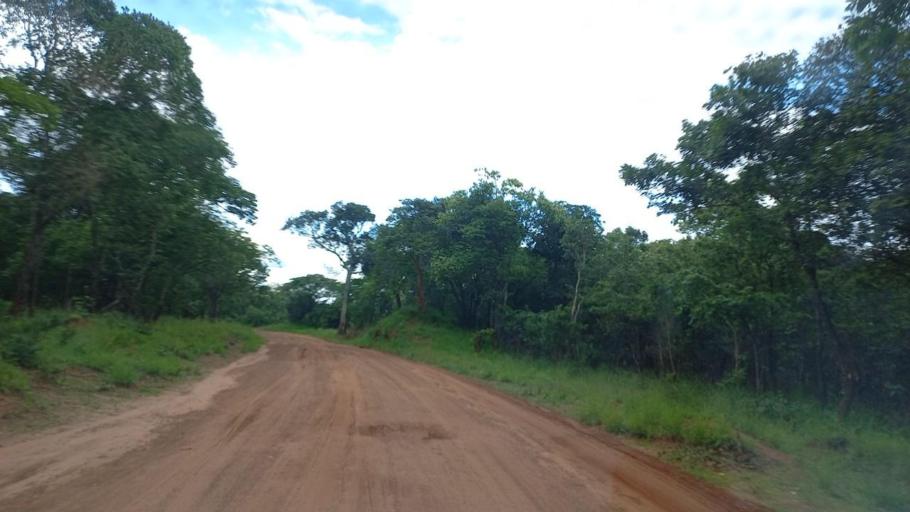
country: ZM
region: North-Western
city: Mwinilunga
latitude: -11.8297
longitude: 24.3715
